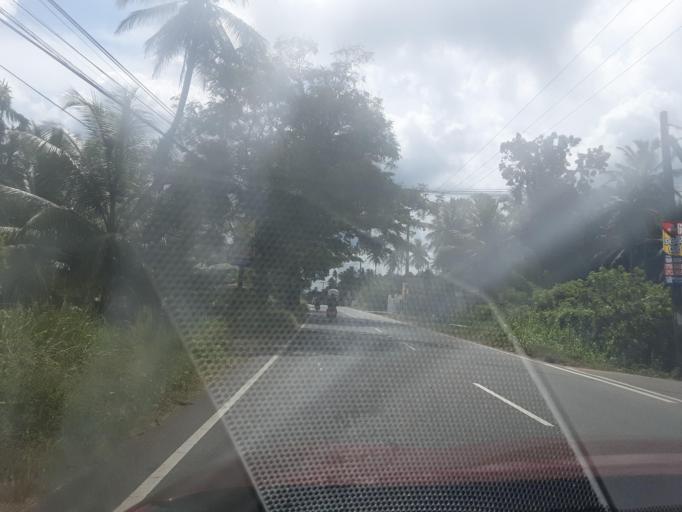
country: LK
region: North Western
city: Kuliyapitiya
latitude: 7.4759
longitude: 80.0102
